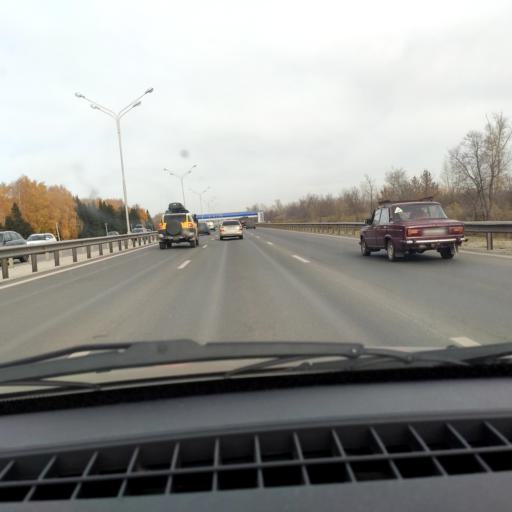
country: RU
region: Bashkortostan
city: Ufa
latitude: 54.6525
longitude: 55.9320
